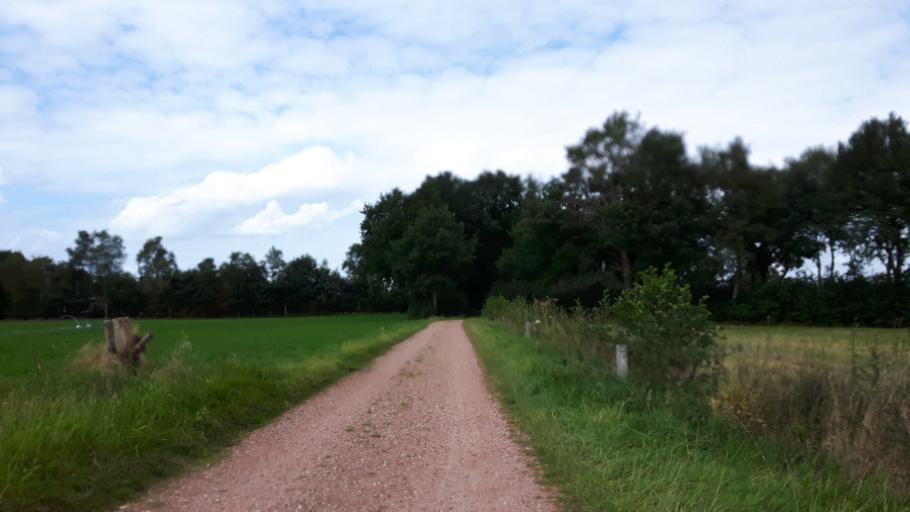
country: NL
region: Groningen
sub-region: Gemeente Leek
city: Leek
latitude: 53.0838
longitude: 6.3220
